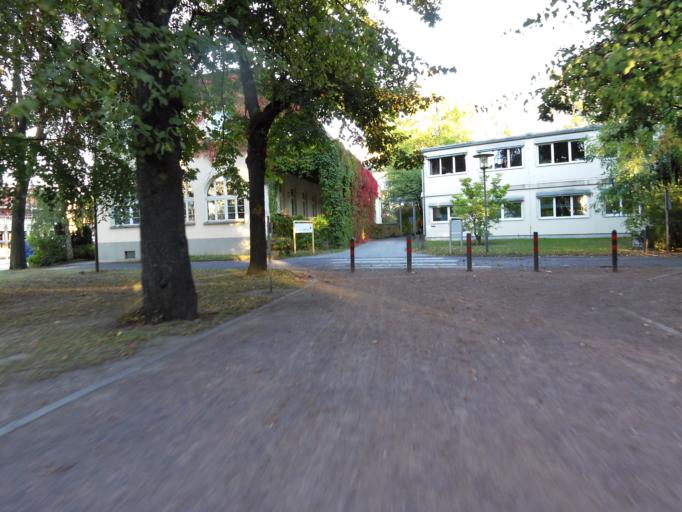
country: DE
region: Saxony
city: Leipzig
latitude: 51.3300
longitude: 12.3892
